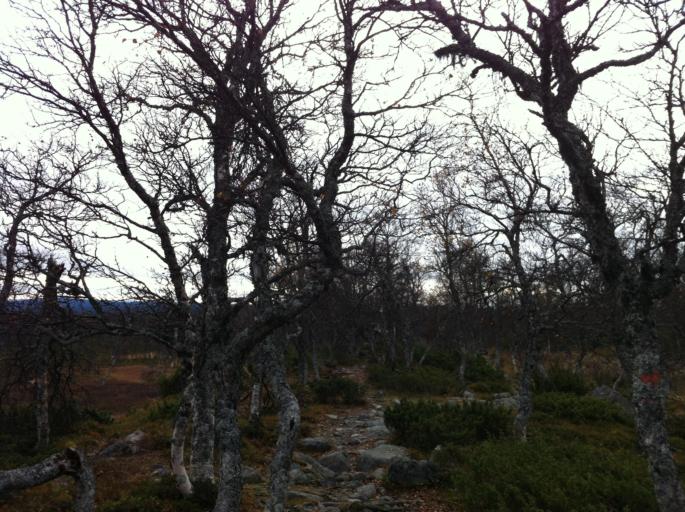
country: NO
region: Hedmark
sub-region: Engerdal
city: Engerdal
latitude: 62.0957
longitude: 12.2652
